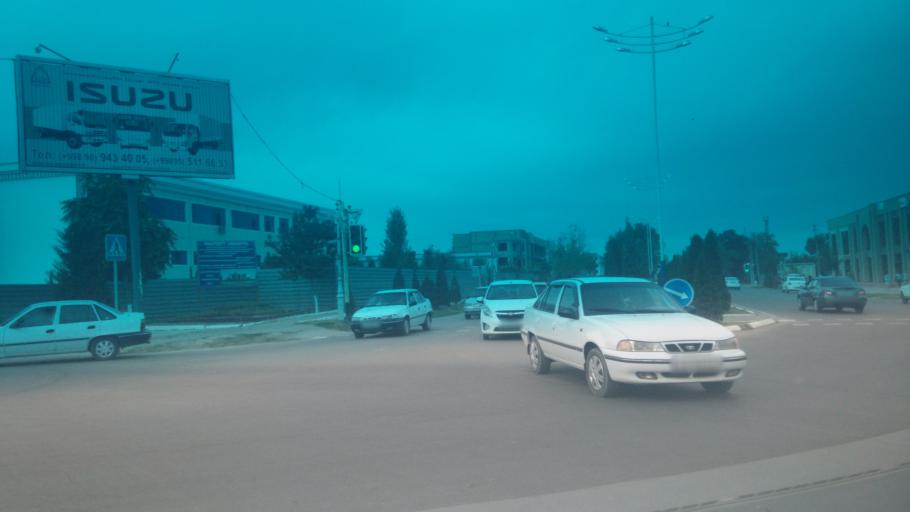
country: UZ
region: Sirdaryo
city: Guliston
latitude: 40.4990
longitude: 68.7745
